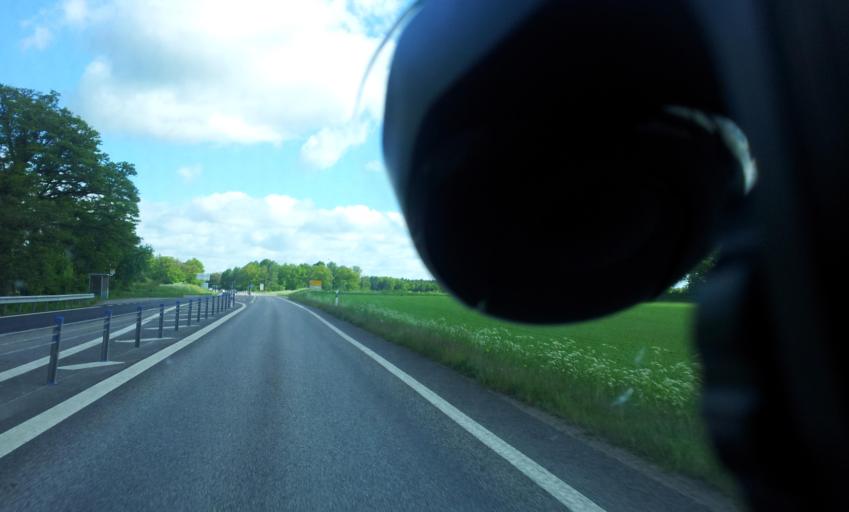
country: SE
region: Kalmar
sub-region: Kalmar Kommun
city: Lindsdal
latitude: 56.8087
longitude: 16.3673
